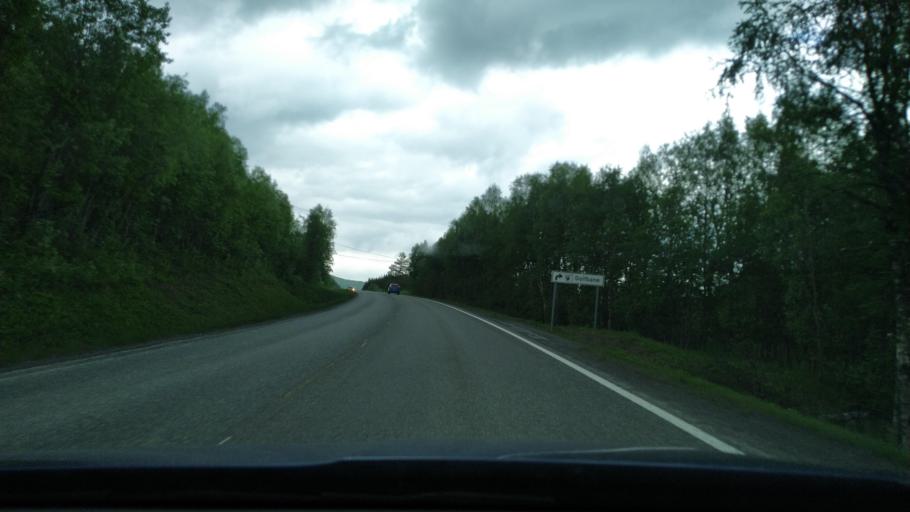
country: NO
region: Troms
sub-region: Malselv
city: Moen
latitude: 68.9866
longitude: 18.5171
